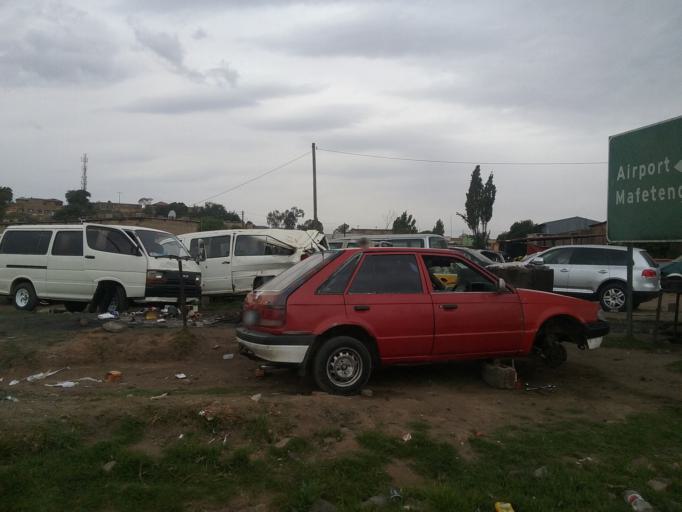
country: LS
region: Maseru
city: Maseru
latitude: -29.3311
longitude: 27.5060
